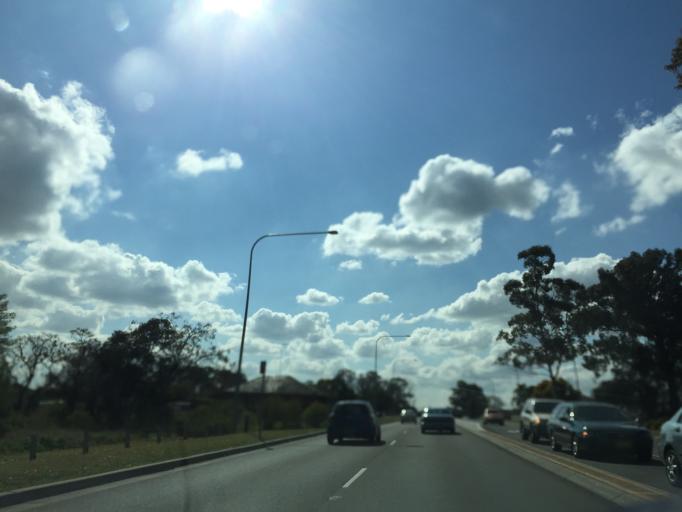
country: AU
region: New South Wales
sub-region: Blacktown
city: Quakers Hill
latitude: -33.7422
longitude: 150.8705
